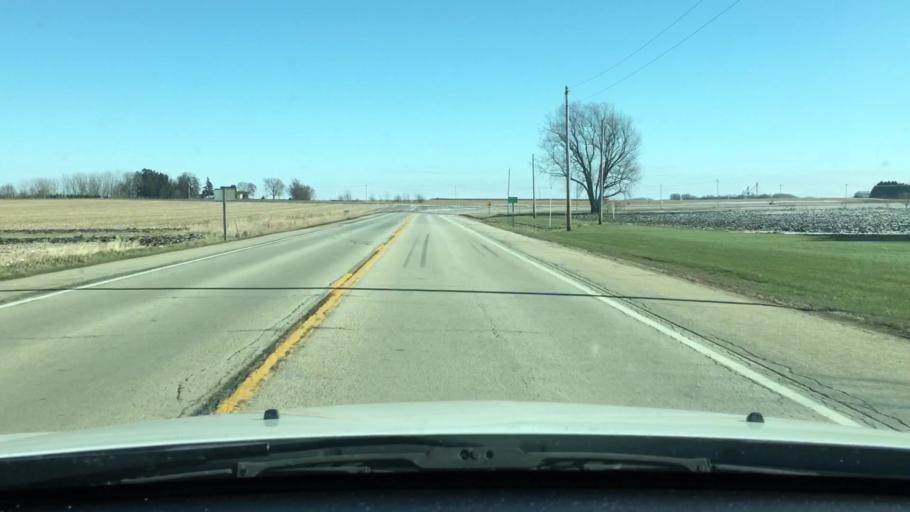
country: US
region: Illinois
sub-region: DeKalb County
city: Malta
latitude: 42.0079
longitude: -88.9439
